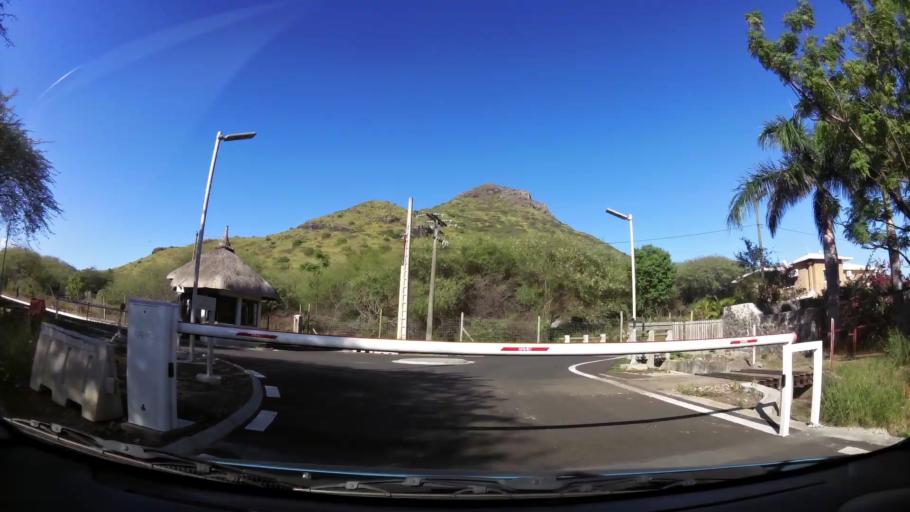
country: MU
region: Black River
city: Tamarin
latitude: -20.3364
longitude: 57.3818
